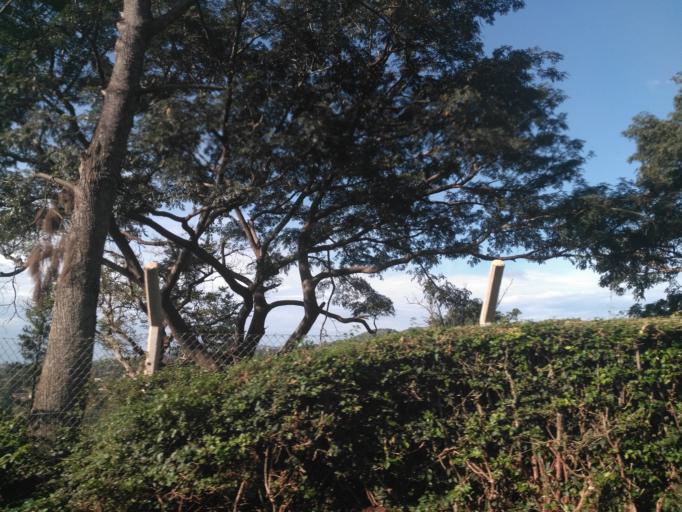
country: UG
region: Eastern Region
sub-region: Jinja District
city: Jinja
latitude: 0.4574
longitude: 33.1800
